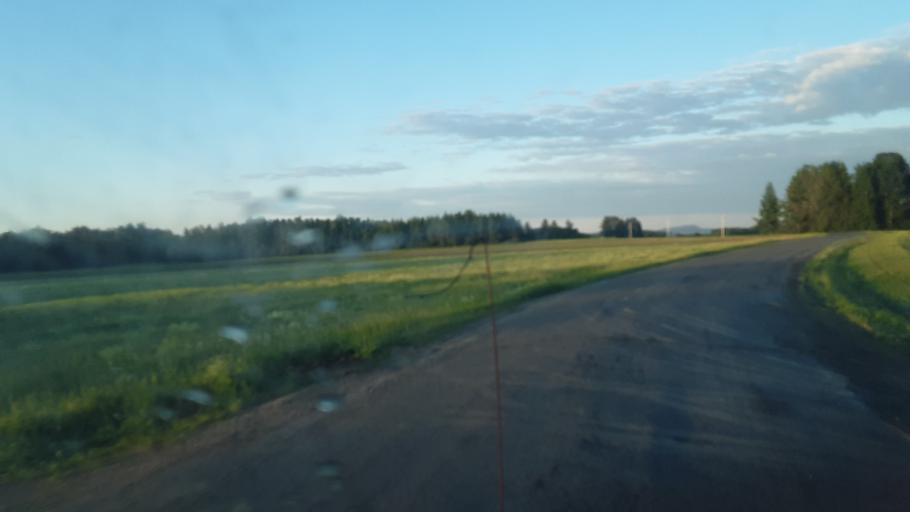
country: US
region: Maine
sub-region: Aroostook County
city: Caribou
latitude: 46.7889
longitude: -68.0977
